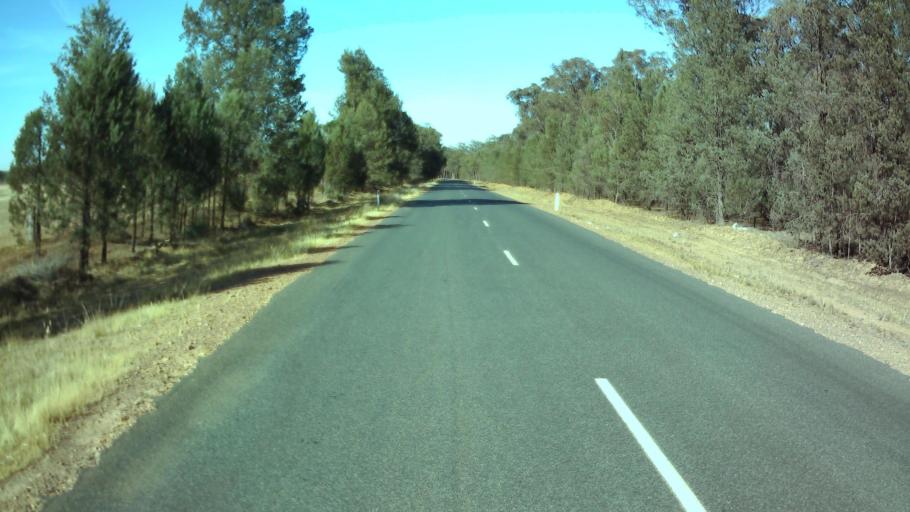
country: AU
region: New South Wales
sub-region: Weddin
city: Grenfell
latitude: -34.0198
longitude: 148.1040
